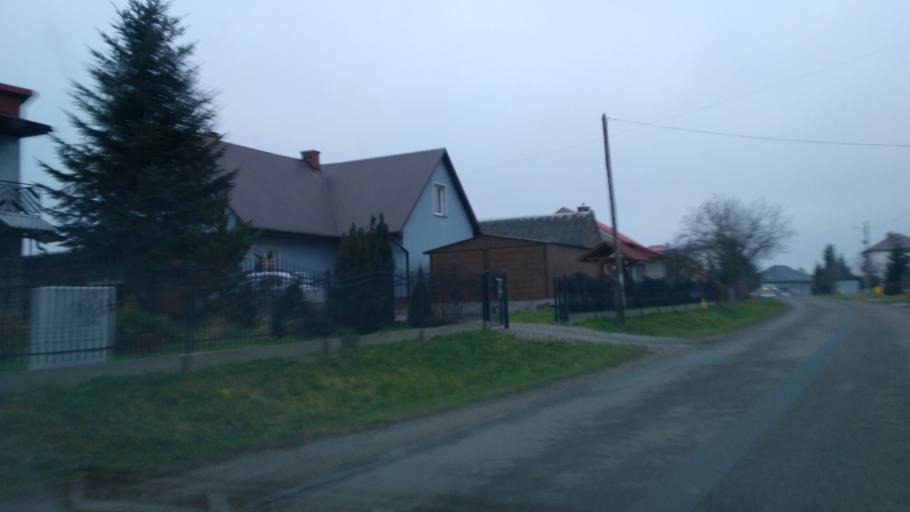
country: PL
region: Subcarpathian Voivodeship
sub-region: Powiat przeworski
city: Rozborz
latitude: 50.0630
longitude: 22.5295
